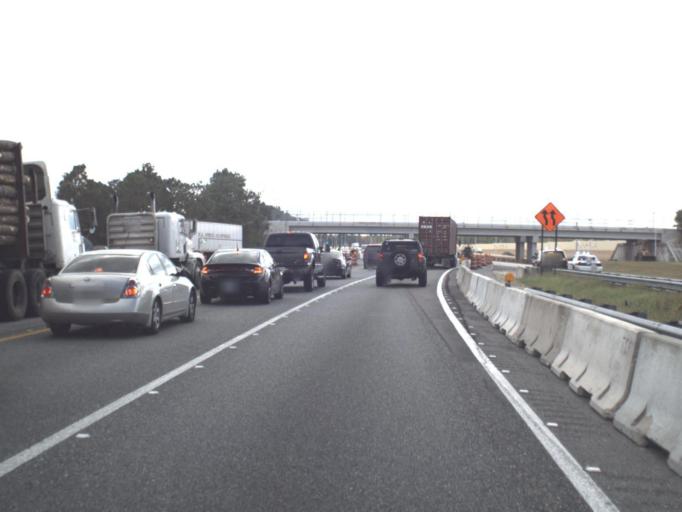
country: US
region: Florida
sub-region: Orange County
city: Southchase
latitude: 28.3679
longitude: -81.3895
